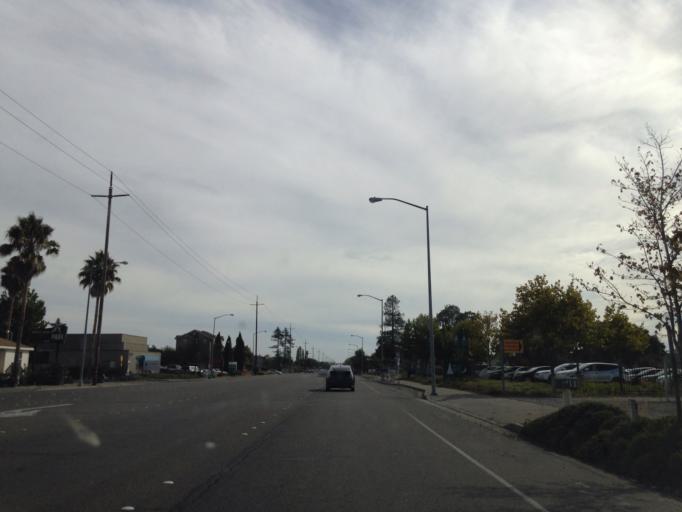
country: US
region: California
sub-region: Sonoma County
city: Roseland
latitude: 38.3994
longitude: -122.7136
